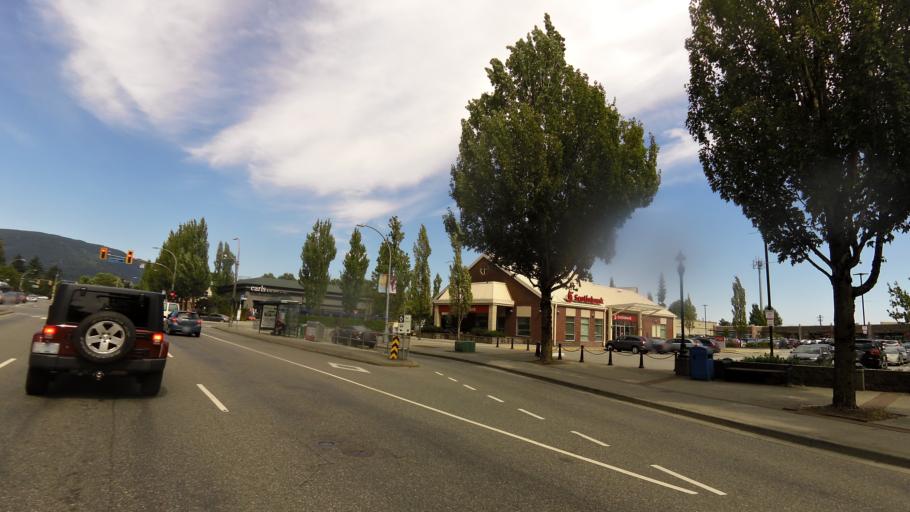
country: CA
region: British Columbia
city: Coquitlam
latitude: 49.2656
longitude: -122.7782
